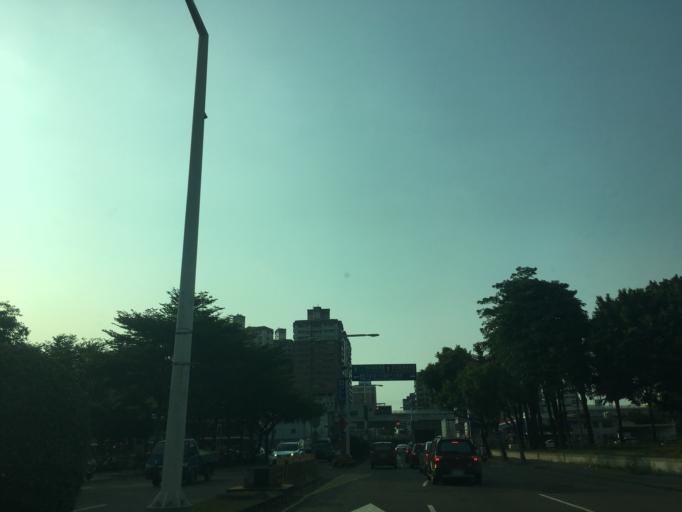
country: TW
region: Taiwan
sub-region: Taichung City
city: Taichung
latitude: 24.1277
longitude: 120.6695
